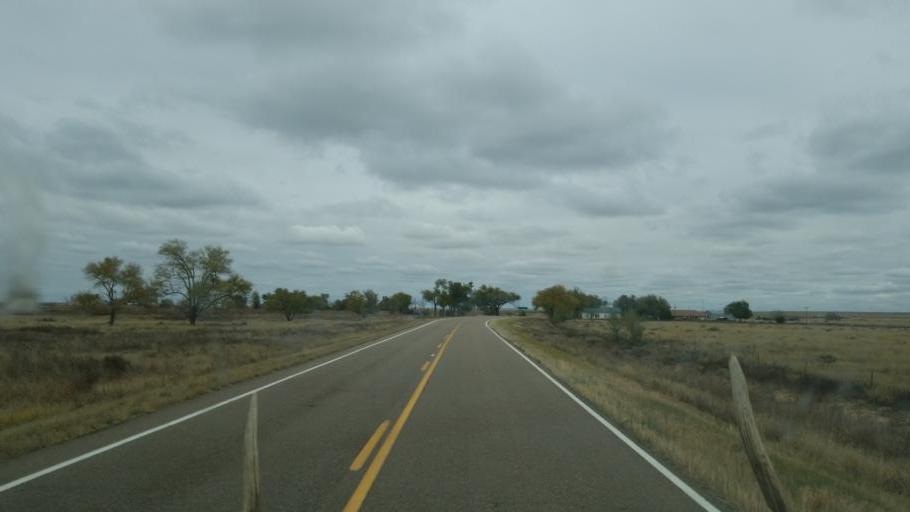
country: US
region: Colorado
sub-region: Bent County
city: Las Animas
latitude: 38.3324
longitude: -103.3445
